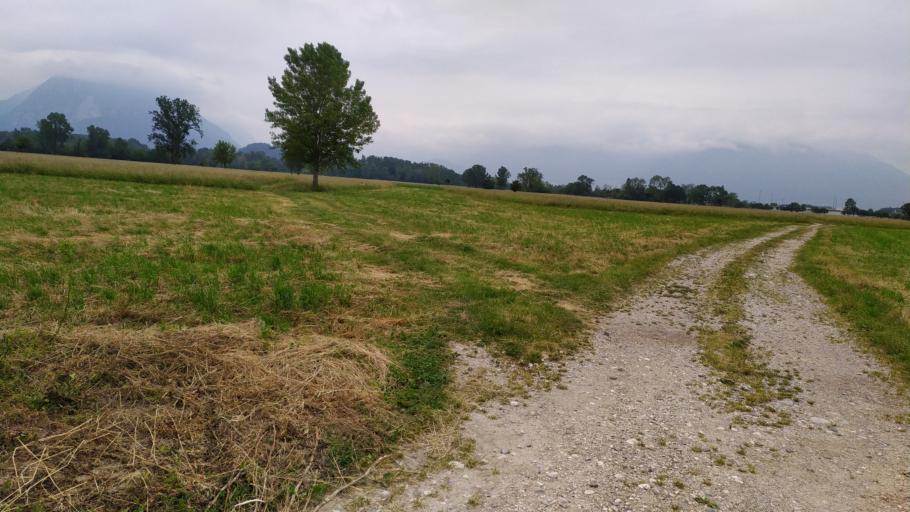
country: IT
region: Friuli Venezia Giulia
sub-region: Provincia di Udine
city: Osoppo
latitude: 46.2341
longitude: 13.0650
